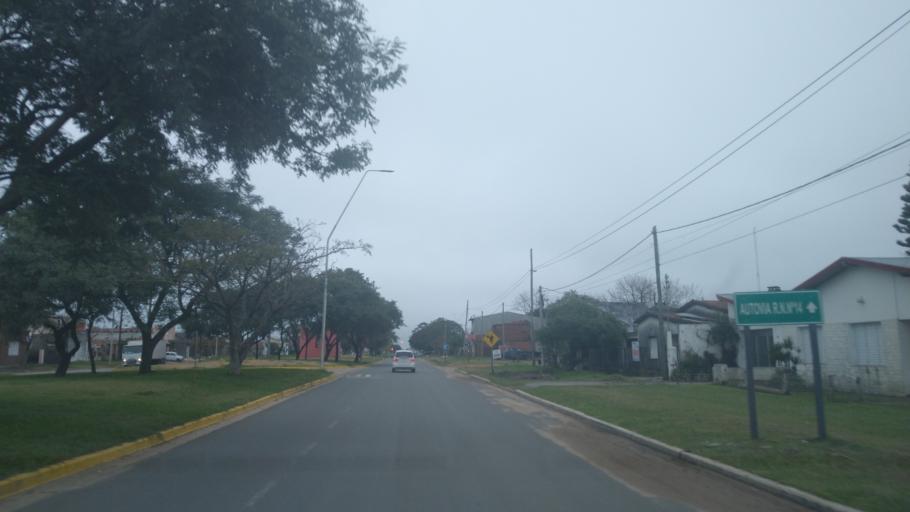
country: AR
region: Entre Rios
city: Chajari
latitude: -30.7603
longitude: -57.9984
